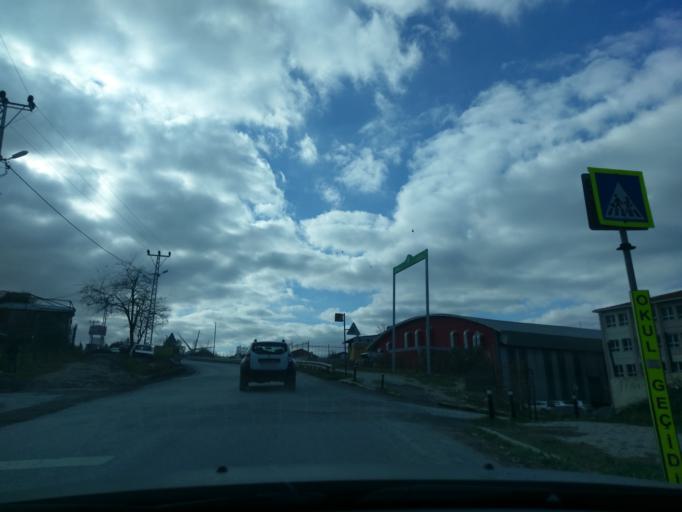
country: TR
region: Istanbul
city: Durusu
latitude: 41.2683
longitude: 28.6901
